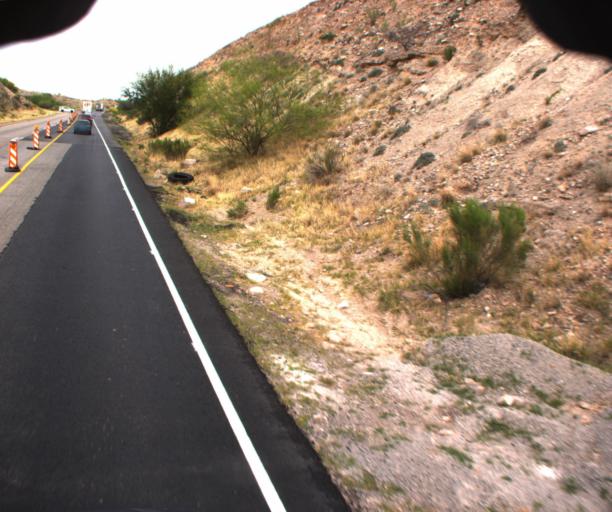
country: US
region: Arizona
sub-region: Pima County
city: Vail
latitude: 31.9974
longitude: -110.6487
